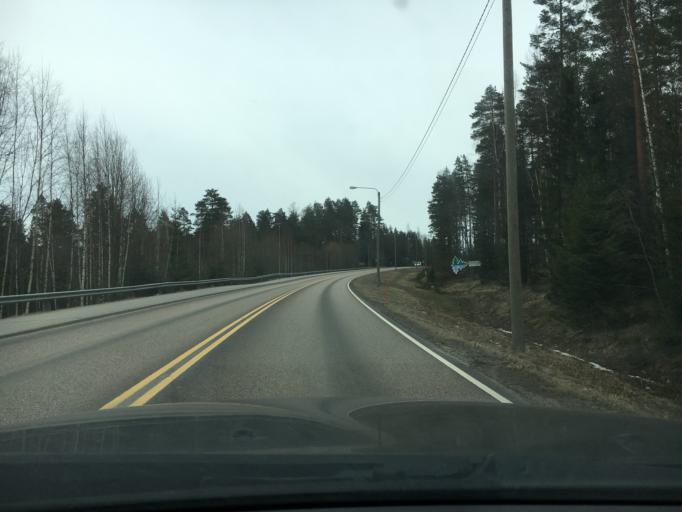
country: FI
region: Central Finland
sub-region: AEaenekoski
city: Konnevesi
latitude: 62.6240
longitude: 26.2702
